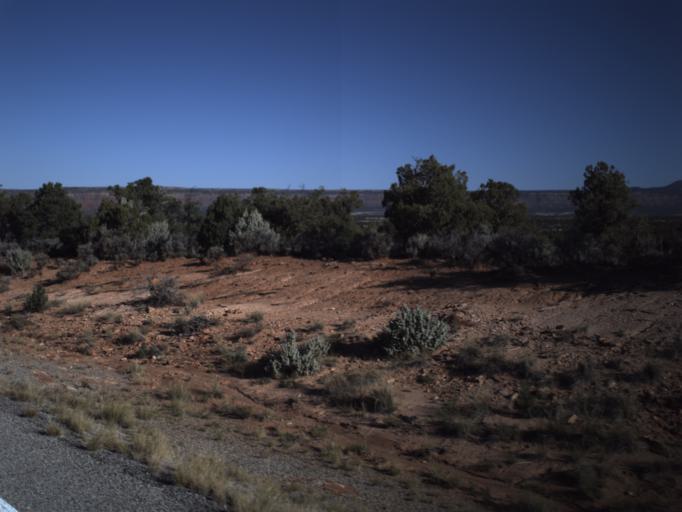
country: US
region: Utah
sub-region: San Juan County
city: Blanding
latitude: 37.5498
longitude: -109.9901
